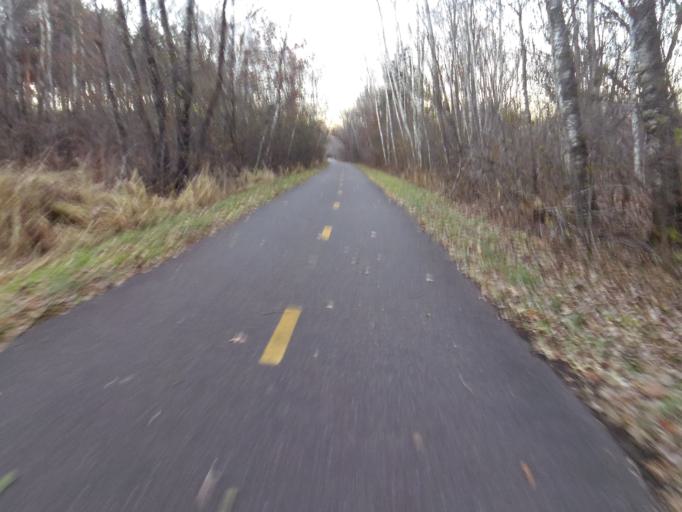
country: US
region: Minnesota
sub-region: Washington County
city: Grant
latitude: 45.0852
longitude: -92.8928
